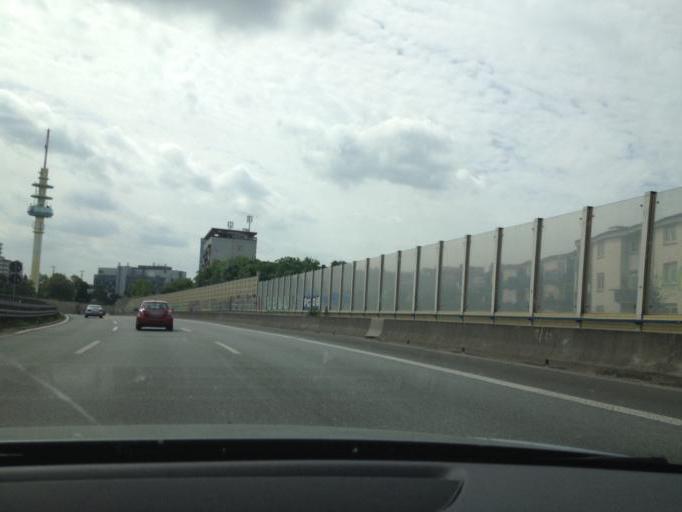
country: DE
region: North Rhine-Westphalia
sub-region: Regierungsbezirk Dusseldorf
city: Duisburg
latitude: 51.4378
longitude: 6.7751
